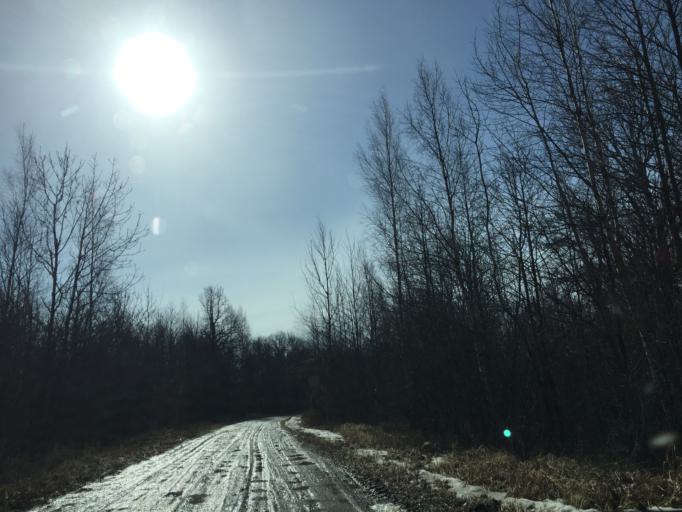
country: EE
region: Laeaene
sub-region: Haapsalu linn
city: Haapsalu
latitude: 58.6569
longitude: 23.5140
